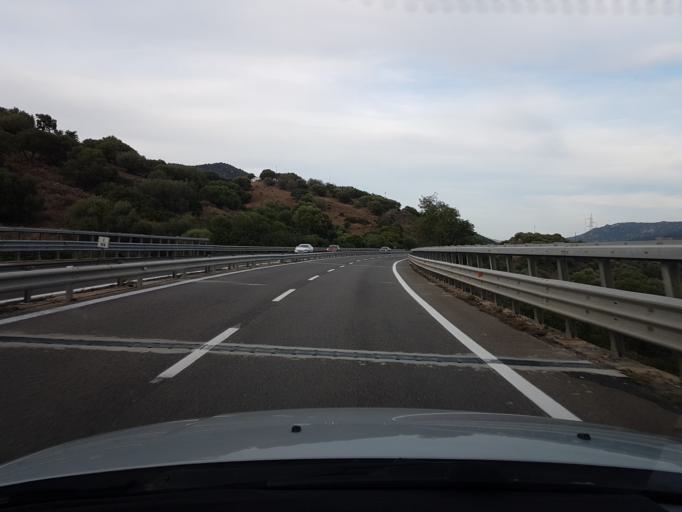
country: IT
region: Sardinia
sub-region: Provincia di Nuoro
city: Orune
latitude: 40.3643
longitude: 9.3642
